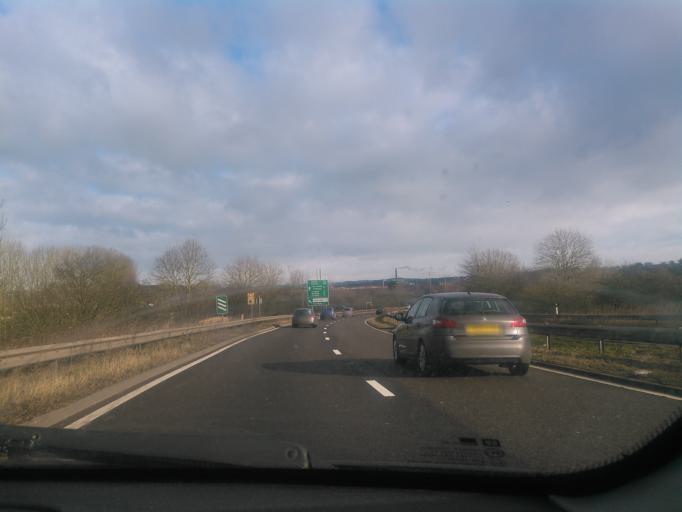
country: GB
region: England
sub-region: Staffordshire
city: Newcastle under Lyme
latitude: 52.9798
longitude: -2.2094
